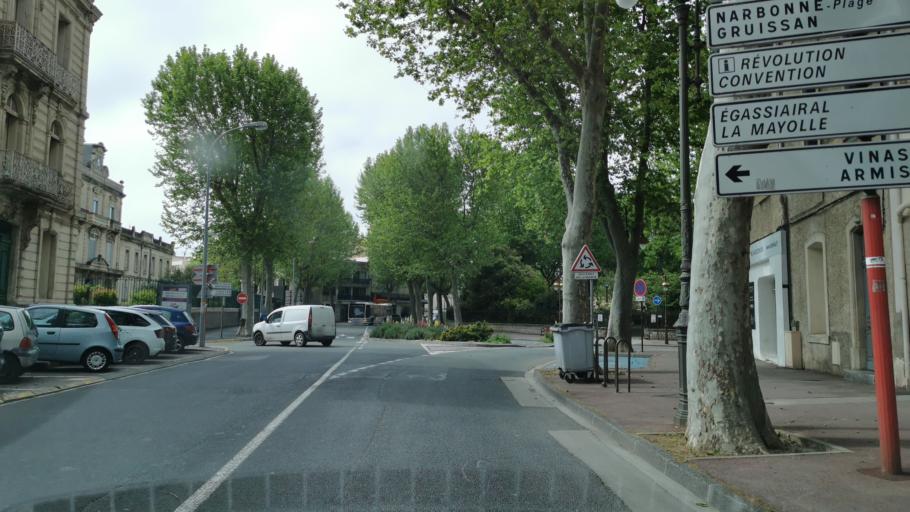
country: FR
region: Languedoc-Roussillon
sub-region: Departement de l'Aude
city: Narbonne
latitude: 43.1883
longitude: 3.0088
